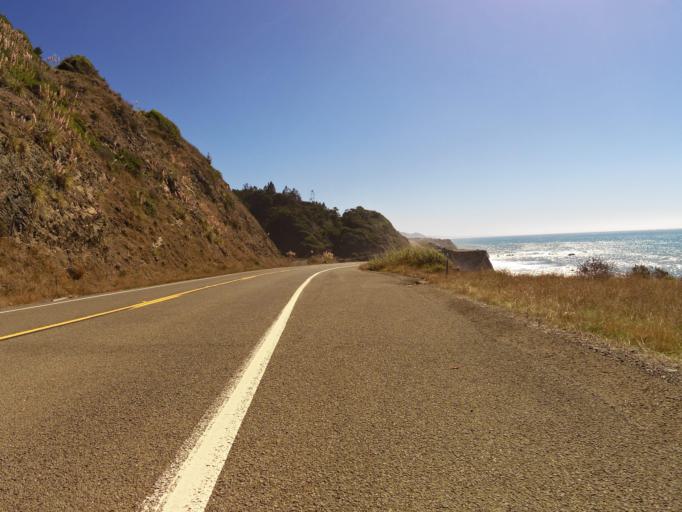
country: US
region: California
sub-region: Mendocino County
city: Fort Bragg
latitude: 39.7054
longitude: -123.8042
